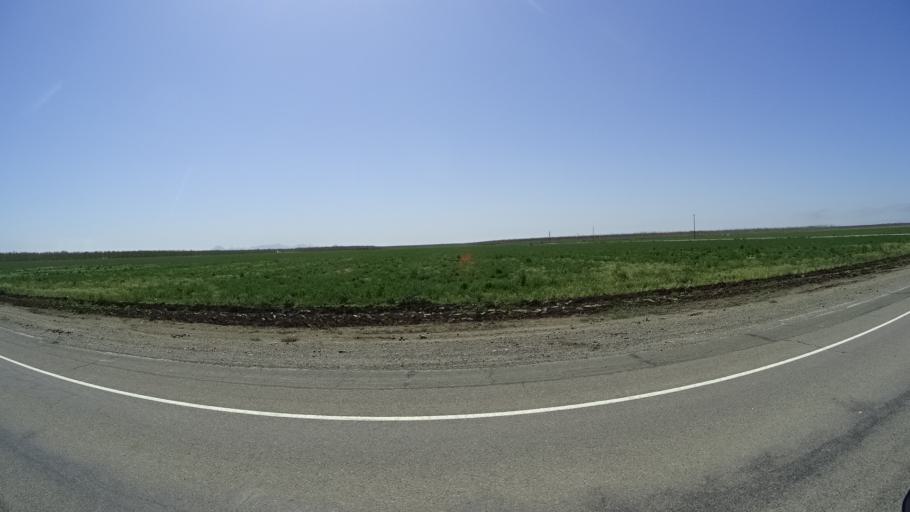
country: US
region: California
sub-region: Butte County
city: Durham
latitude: 39.4642
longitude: -121.9477
